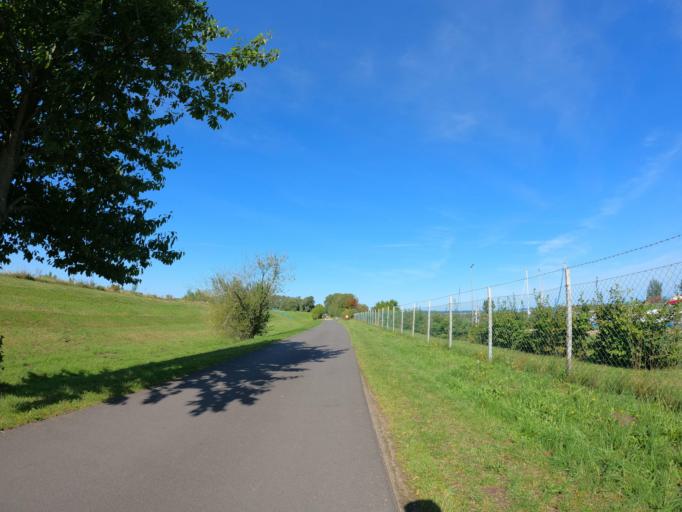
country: DE
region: Mecklenburg-Vorpommern
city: Prohn
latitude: 54.3798
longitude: 13.0466
